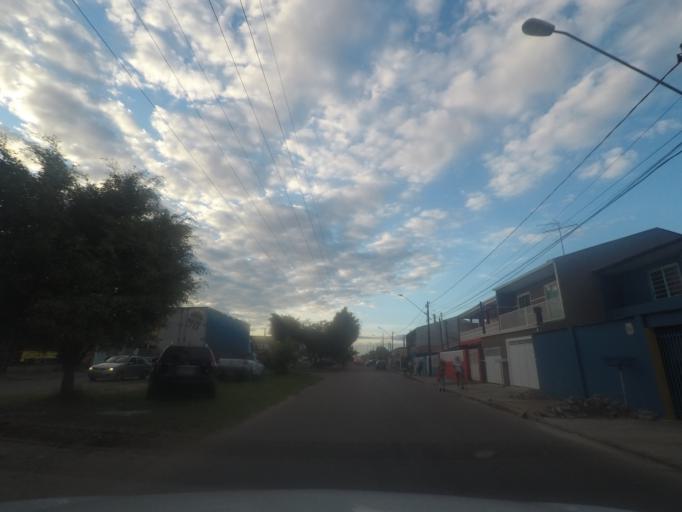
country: BR
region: Parana
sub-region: Pinhais
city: Pinhais
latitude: -25.4628
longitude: -49.1963
